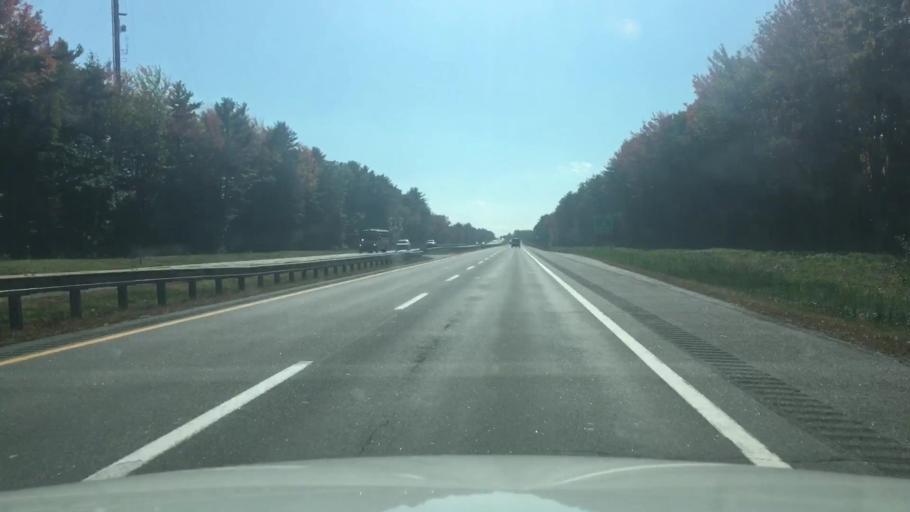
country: US
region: Maine
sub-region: Cumberland County
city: Westbrook
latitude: 43.7076
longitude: -70.3108
